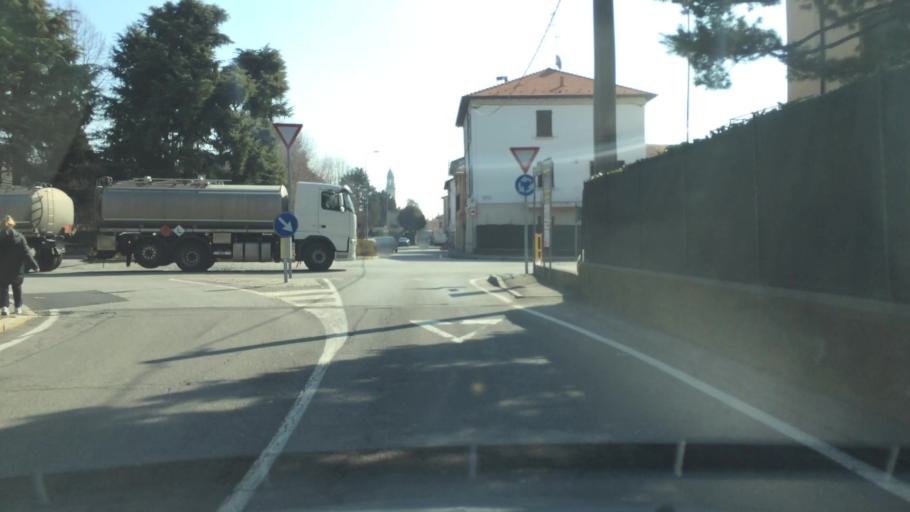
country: IT
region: Lombardy
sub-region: Provincia di Como
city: Lomazzo
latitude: 45.6988
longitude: 9.0316
